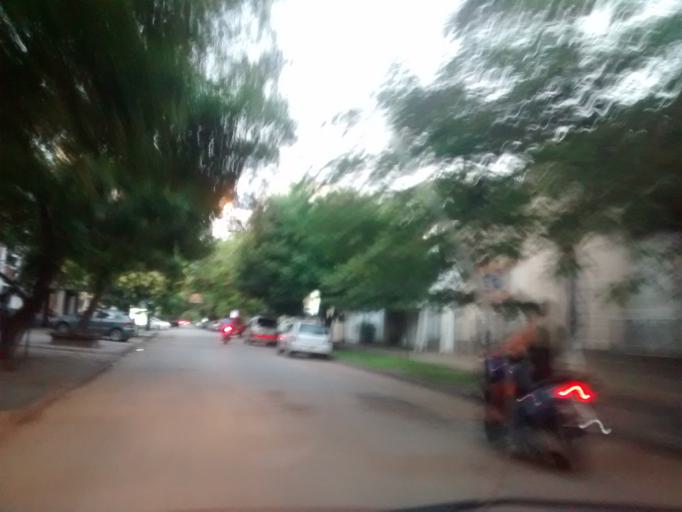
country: AR
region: Chaco
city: Resistencia
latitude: -27.4524
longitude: -58.9827
